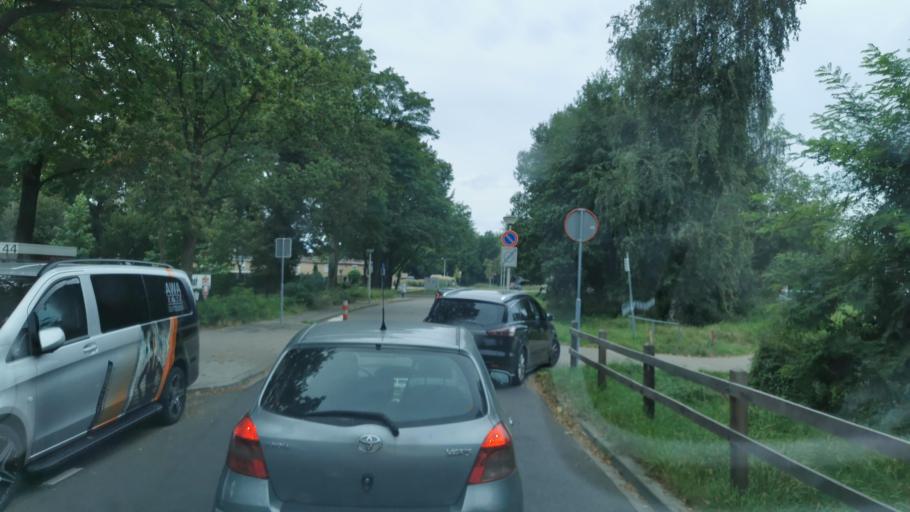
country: NL
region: Overijssel
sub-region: Gemeente Enschede
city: Enschede
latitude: 52.2332
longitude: 6.9088
